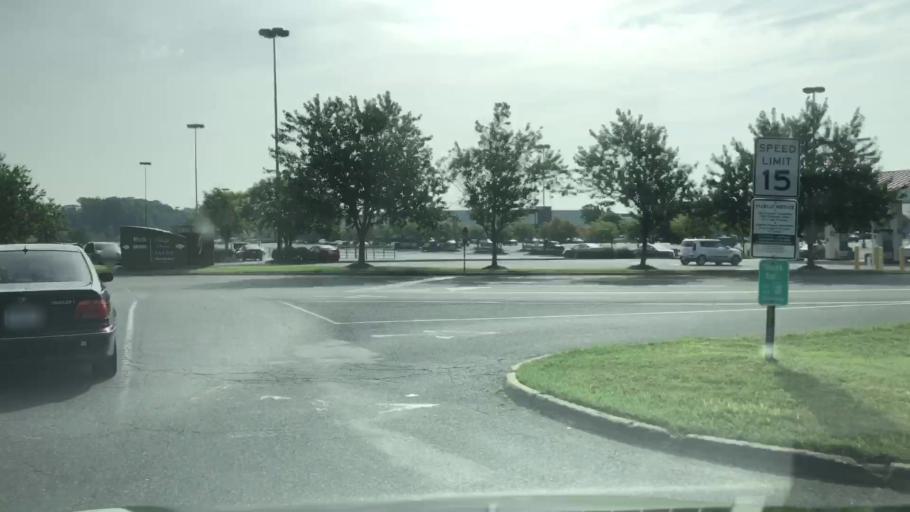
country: US
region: Virginia
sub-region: City of Fredericksburg
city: Fredericksburg
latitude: 38.2922
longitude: -77.5177
